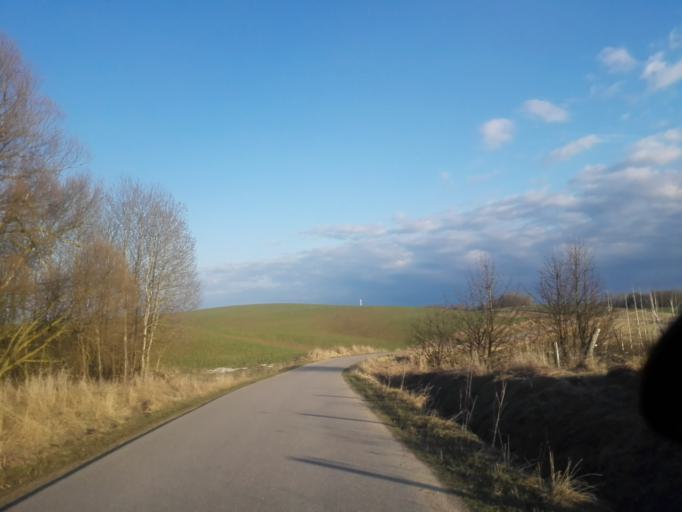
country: PL
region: Podlasie
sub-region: Suwalki
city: Suwalki
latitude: 54.2111
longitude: 23.0068
